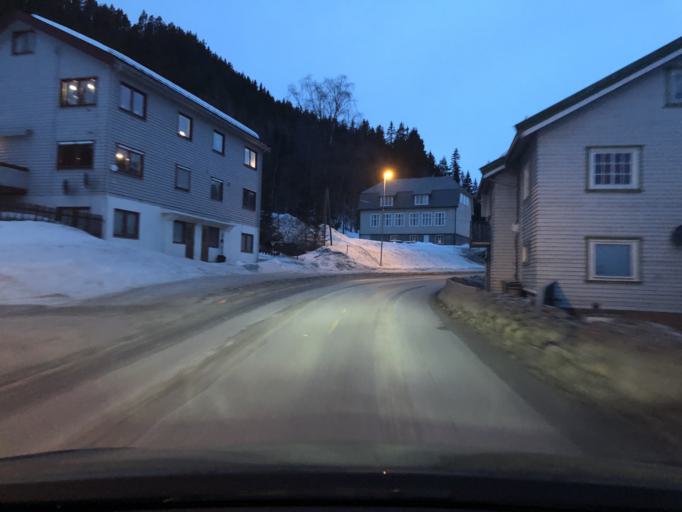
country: NO
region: Oppland
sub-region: Nord-Aurdal
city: Fagernes
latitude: 60.9857
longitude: 9.2271
